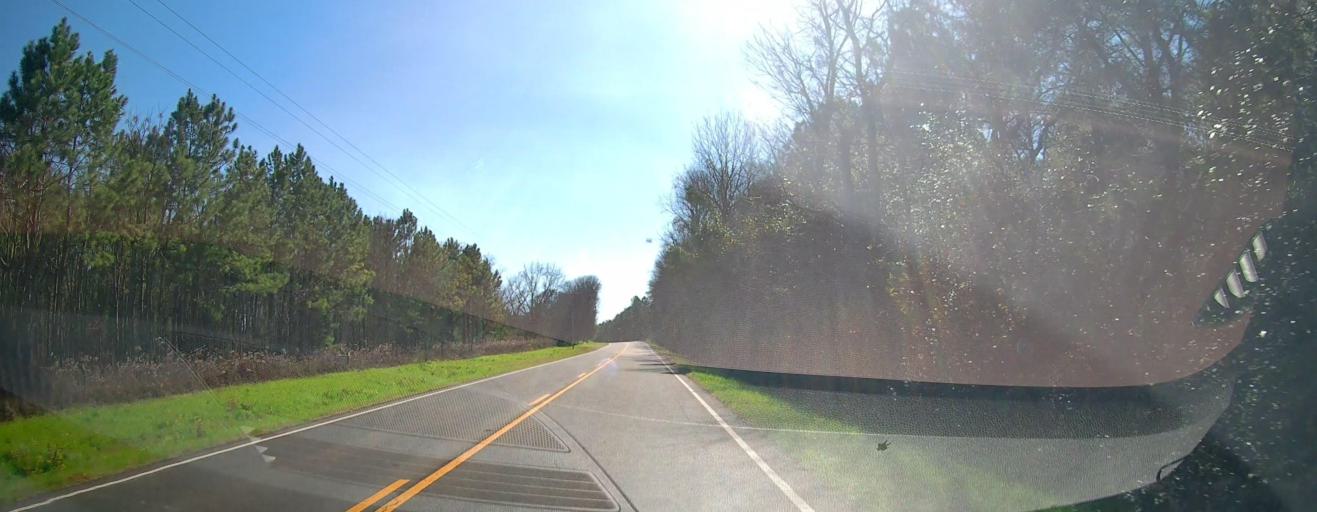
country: US
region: Georgia
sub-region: Macon County
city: Montezuma
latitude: 32.3574
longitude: -84.0160
